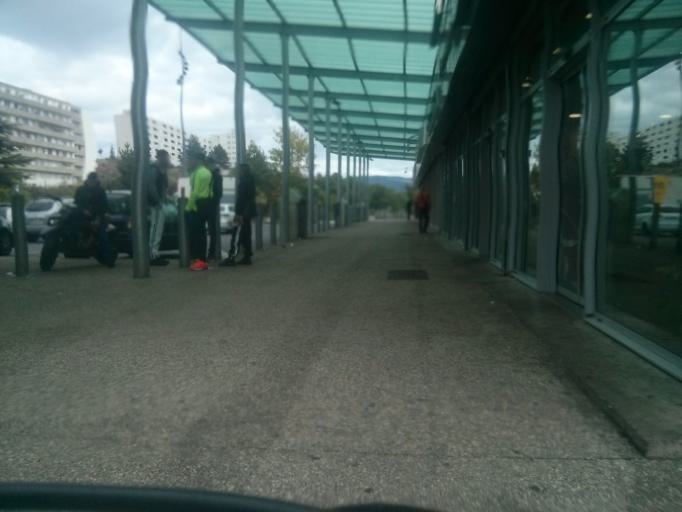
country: FR
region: Rhone-Alpes
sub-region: Departement de la Loire
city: La Tour-en-Jarez
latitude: 45.4706
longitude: 4.3997
